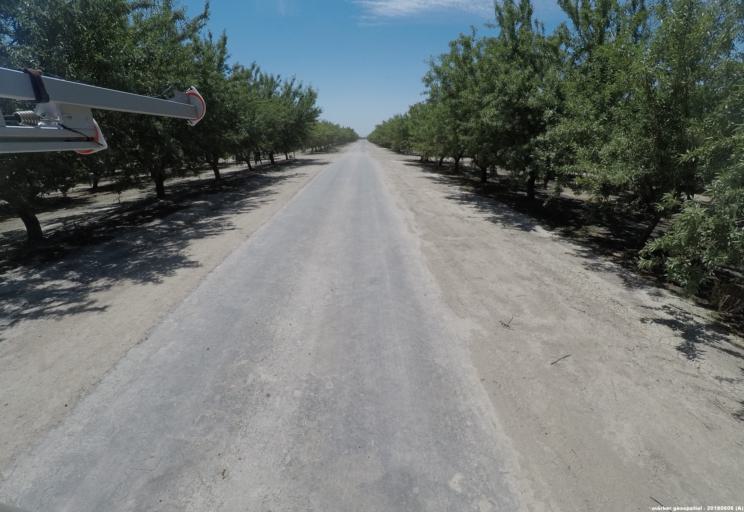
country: US
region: California
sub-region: Fresno County
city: Firebaugh
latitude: 36.8538
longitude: -120.3909
